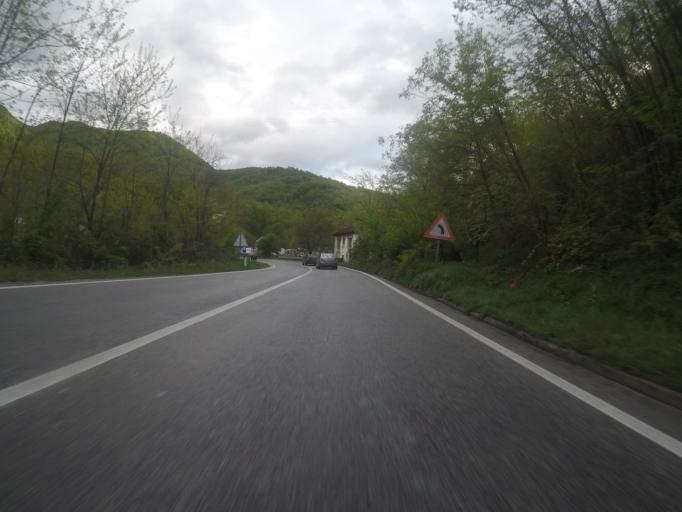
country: BA
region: Federation of Bosnia and Herzegovina
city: Konjic
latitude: 43.6886
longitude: 17.8720
